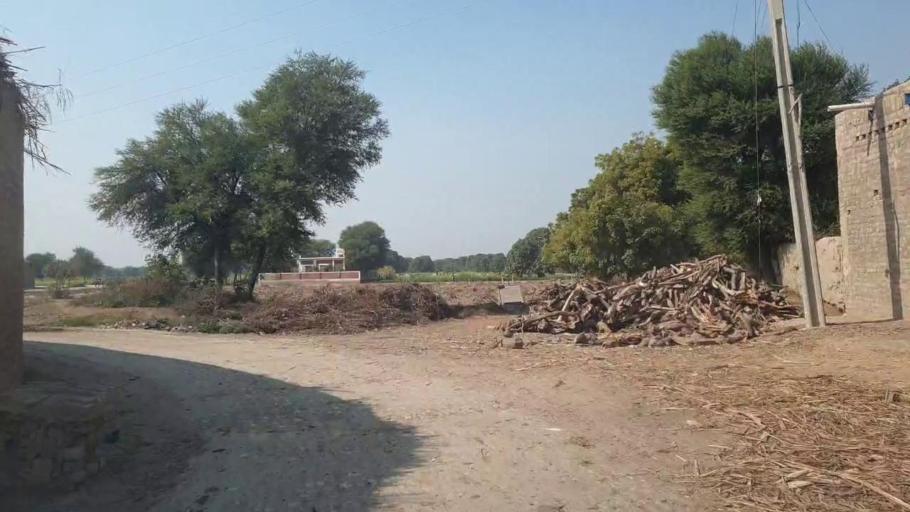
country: PK
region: Sindh
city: Tando Jam
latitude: 25.3328
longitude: 68.6261
